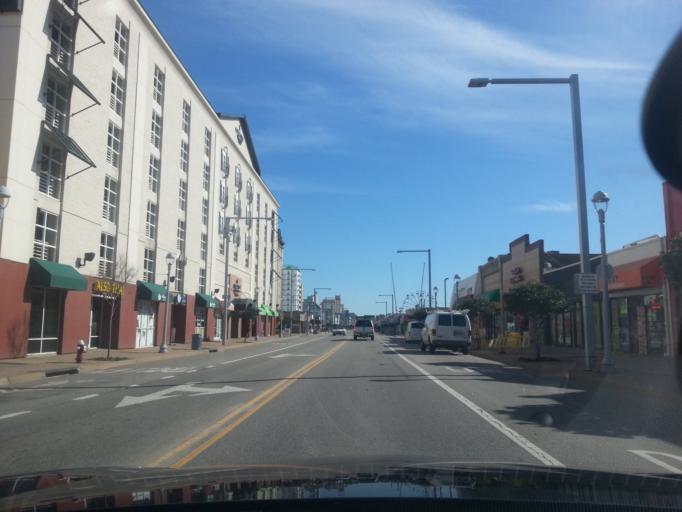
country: US
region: Virginia
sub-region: City of Virginia Beach
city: Virginia Beach
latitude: 36.8472
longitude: -75.9748
